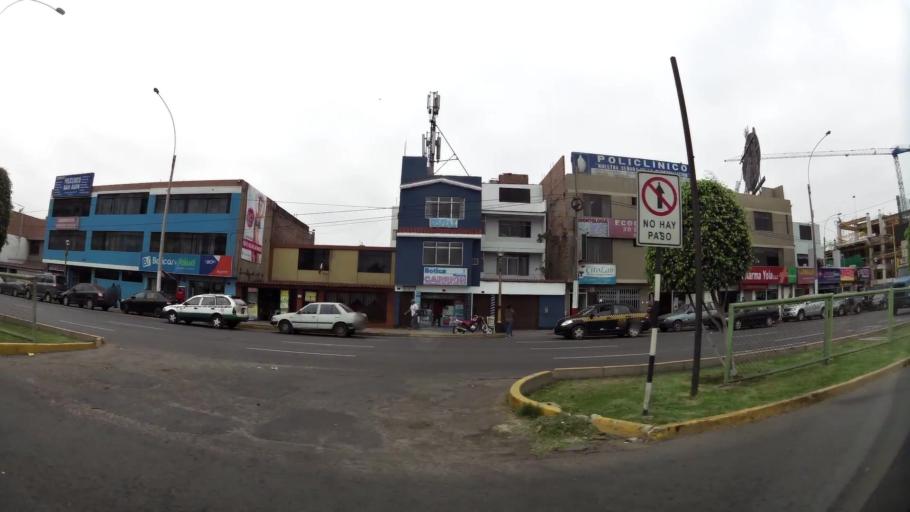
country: PE
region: Callao
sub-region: Callao
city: Callao
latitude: -12.0628
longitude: -77.1229
